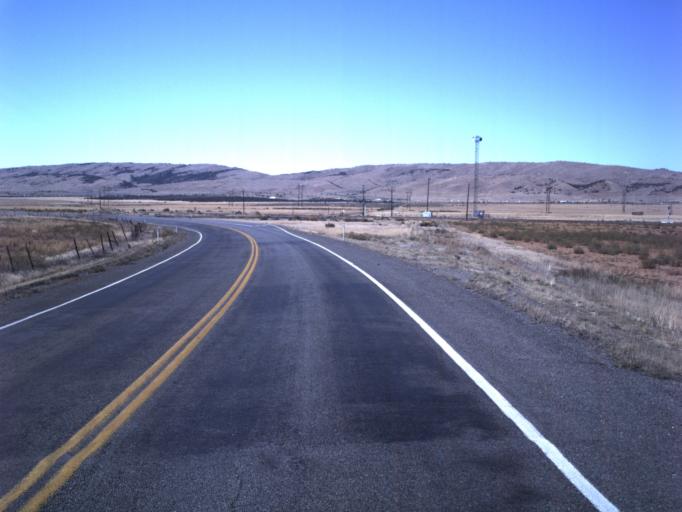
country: US
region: Utah
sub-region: Juab County
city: Nephi
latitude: 39.5577
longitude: -111.9164
